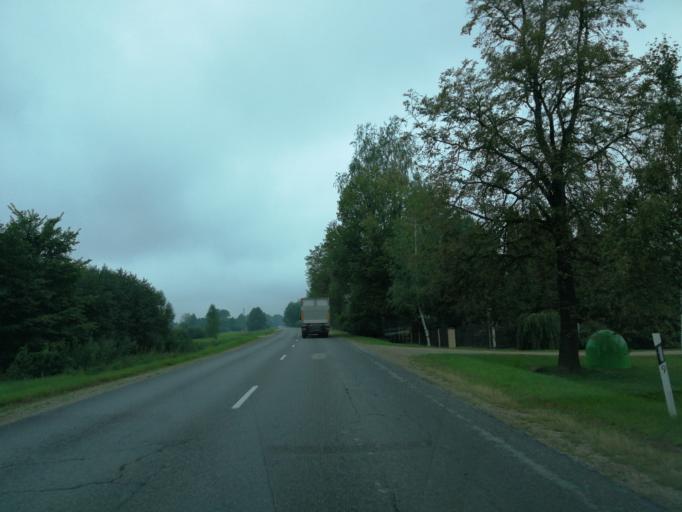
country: LV
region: Livani
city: Livani
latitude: 56.3441
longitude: 26.3321
